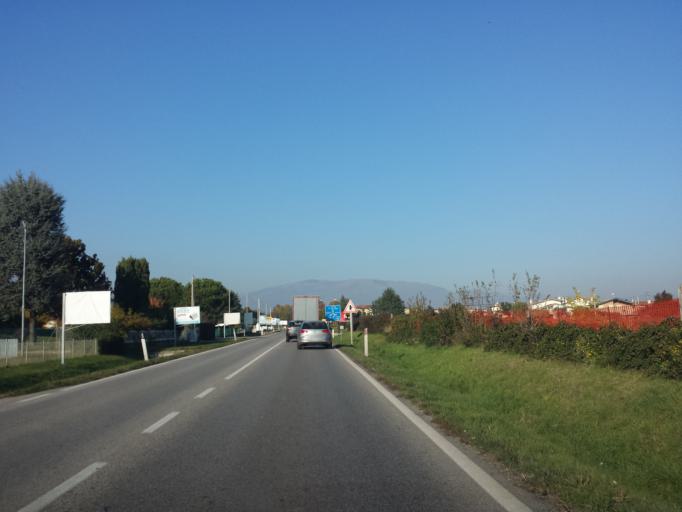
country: IT
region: Veneto
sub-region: Provincia di Treviso
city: Caerano di San Marco
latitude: 45.7818
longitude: 11.9937
